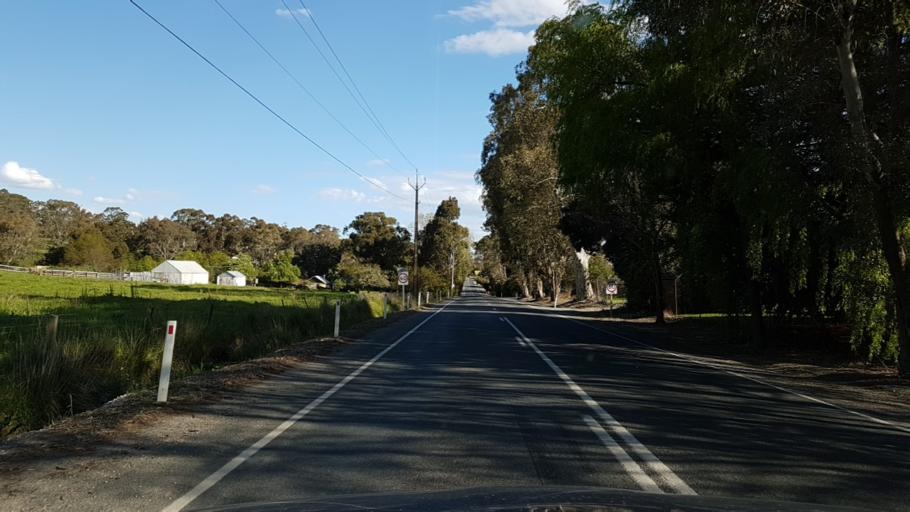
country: AU
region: South Australia
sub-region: Adelaide Hills
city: Lobethal
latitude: -34.8919
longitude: 138.8794
